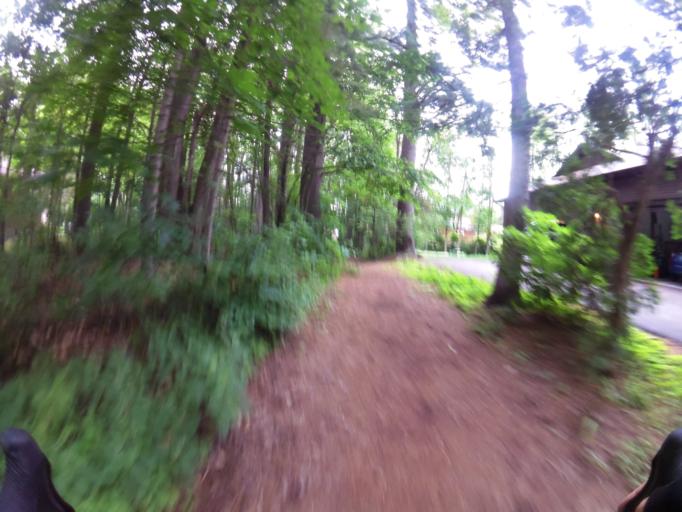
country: CA
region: Ontario
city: Ottawa
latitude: 45.3223
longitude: -75.7127
